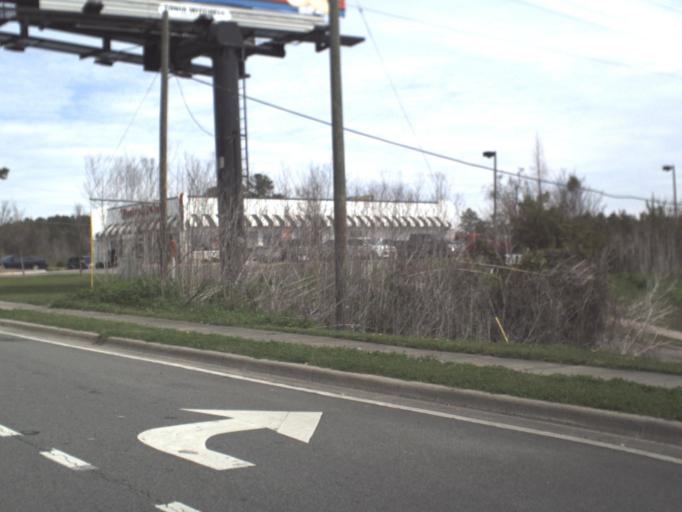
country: US
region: Florida
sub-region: Leon County
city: Tallahassee
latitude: 30.4622
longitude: -84.3610
